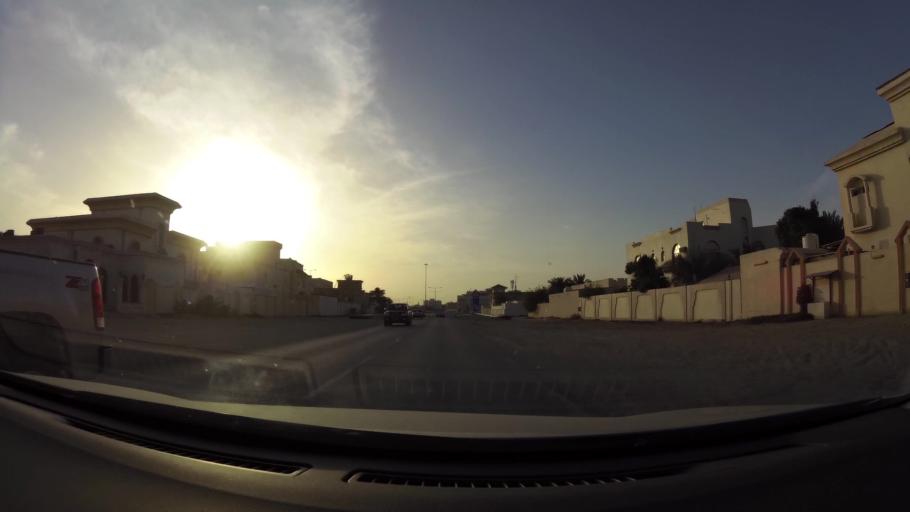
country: QA
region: Al Wakrah
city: Al Wakrah
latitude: 25.1496
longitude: 51.6049
